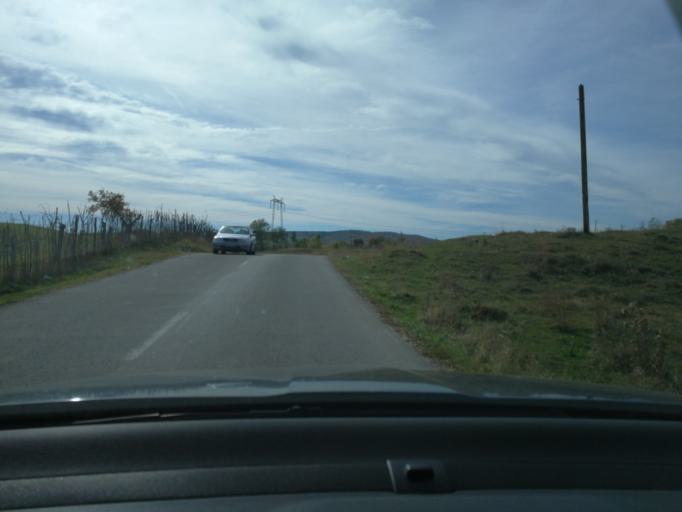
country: RO
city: Brebu Manastirei
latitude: 45.1960
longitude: 25.7748
